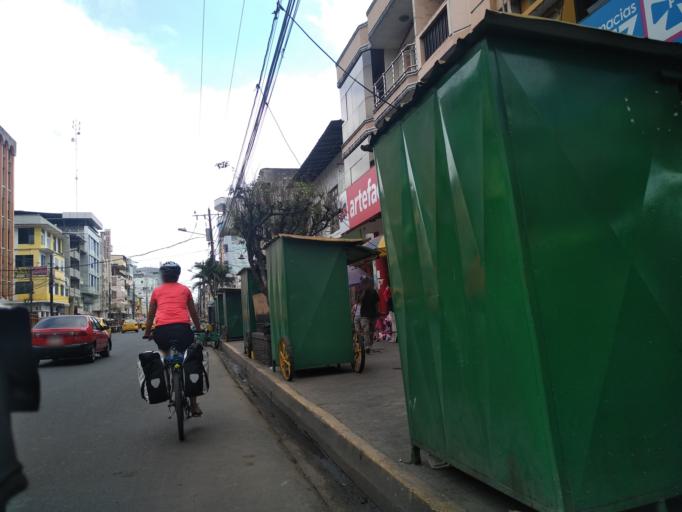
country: EC
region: Los Rios
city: Quevedo
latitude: -1.0255
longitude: -79.4670
